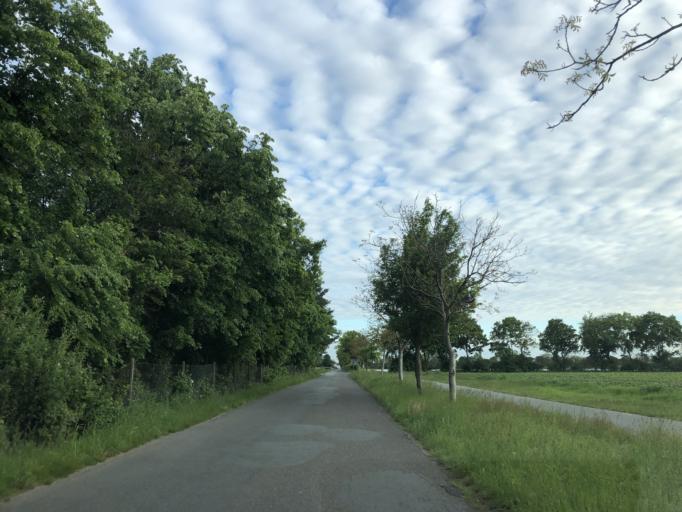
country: DE
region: Hesse
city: Weiterstadt
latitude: 49.9420
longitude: 8.6033
